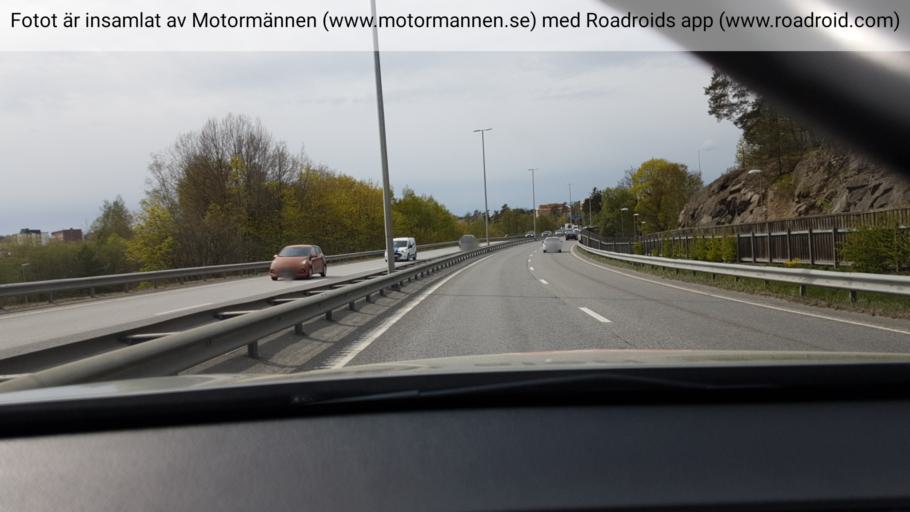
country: SE
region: Stockholm
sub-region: Huddinge Kommun
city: Huddinge
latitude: 59.2426
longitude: 17.9854
